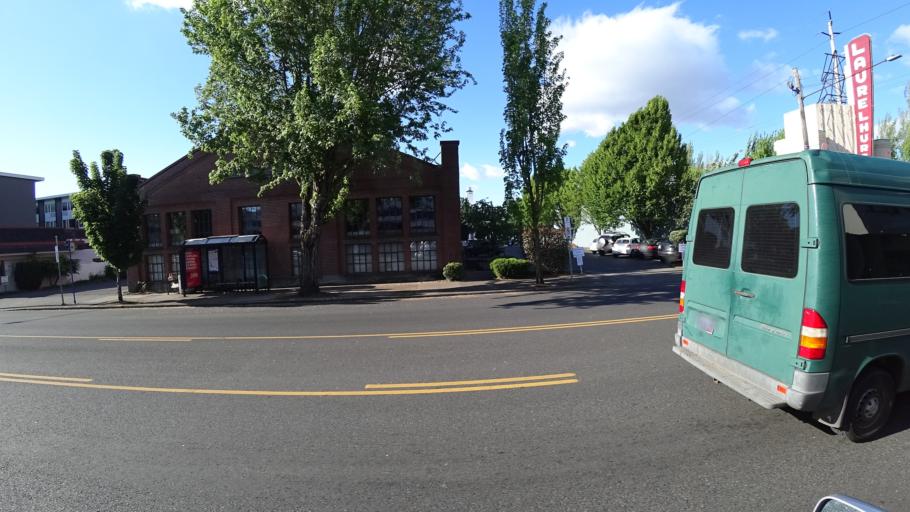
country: US
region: Oregon
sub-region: Multnomah County
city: Portland
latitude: 45.5228
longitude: -122.6379
